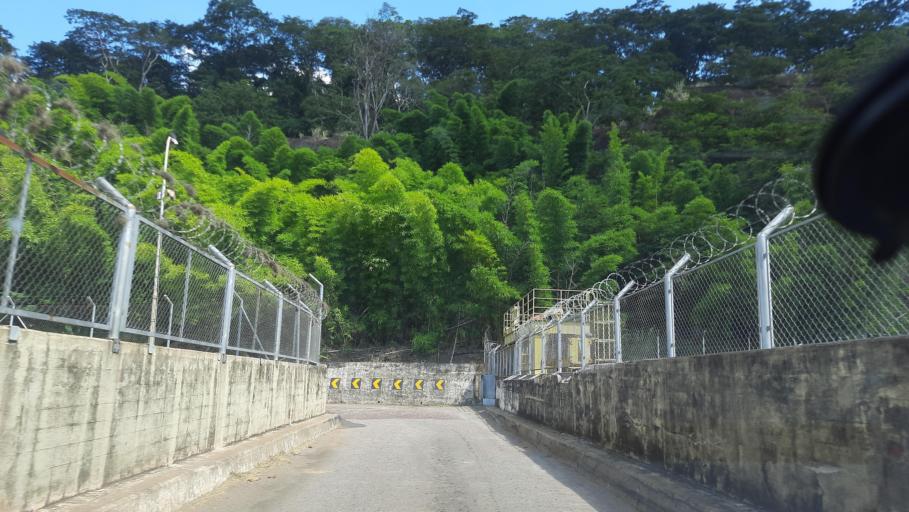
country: BR
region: Sao Paulo
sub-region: Sao Jose Do Rio Pardo
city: Sao Jose do Rio Pardo
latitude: -21.6046
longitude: -46.9486
